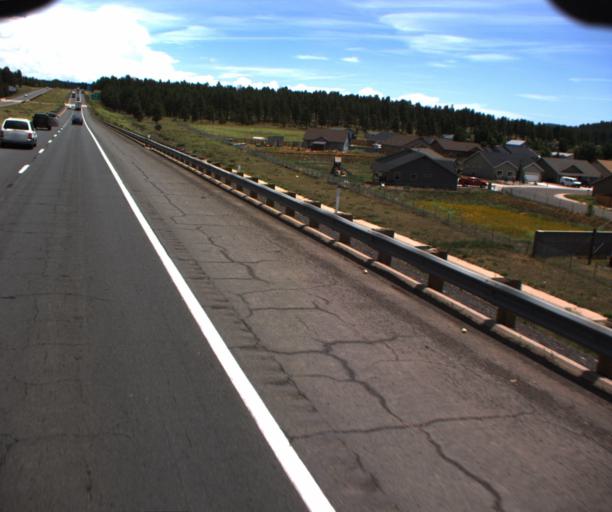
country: US
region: Arizona
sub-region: Coconino County
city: Williams
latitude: 35.2638
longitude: -112.1773
